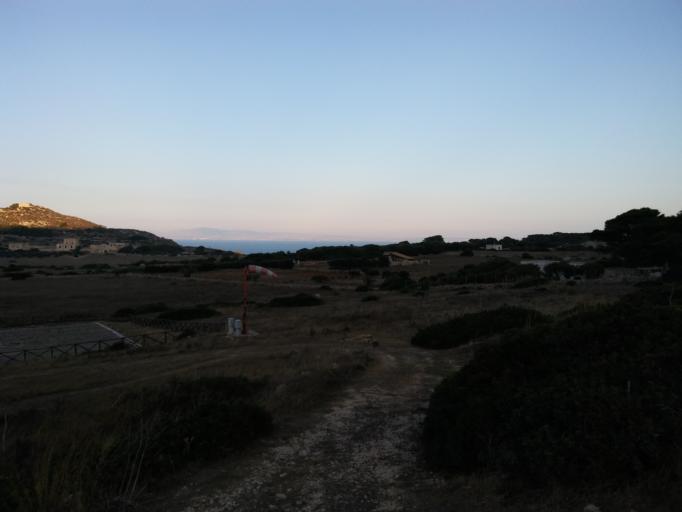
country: IT
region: Sicily
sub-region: Trapani
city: Favignana
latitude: 37.9928
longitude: 12.3378
